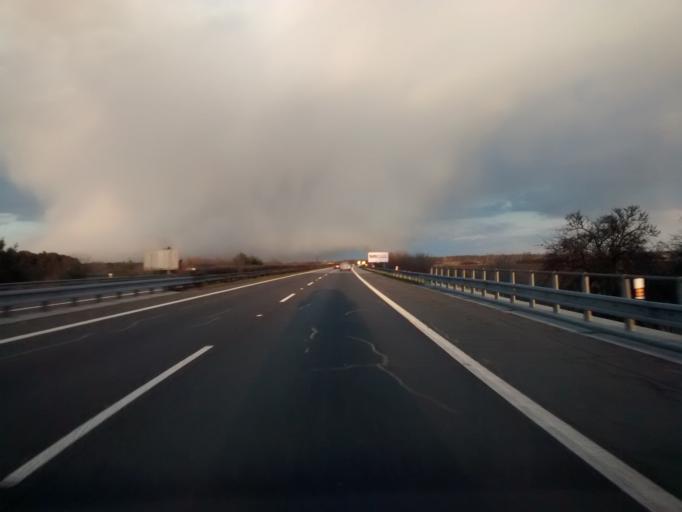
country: CZ
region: Central Bohemia
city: Pecky
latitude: 50.1231
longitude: 15.0406
